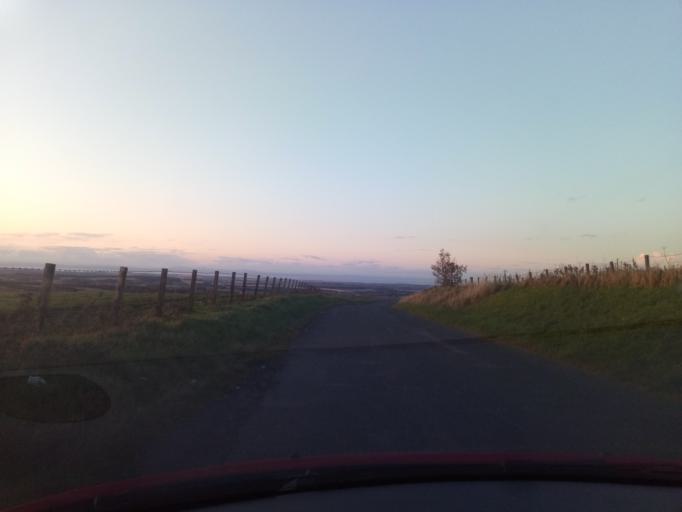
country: GB
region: Scotland
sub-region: East Lothian
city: Pencaitland
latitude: 55.8159
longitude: -2.8755
